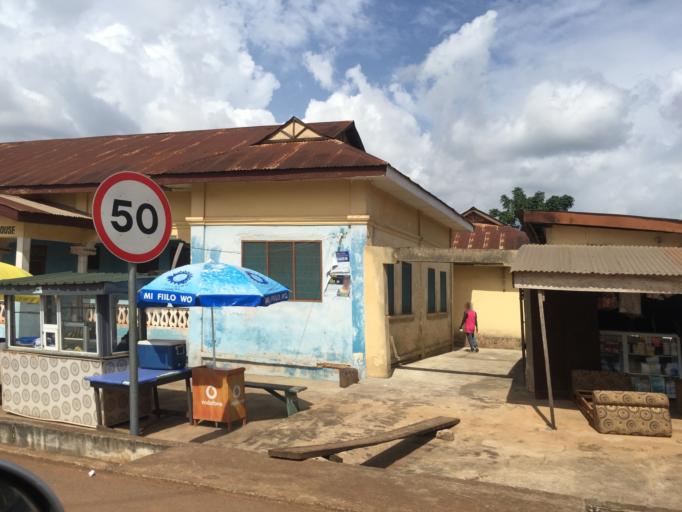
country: GH
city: Mpraeso
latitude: 6.5872
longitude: -0.7364
